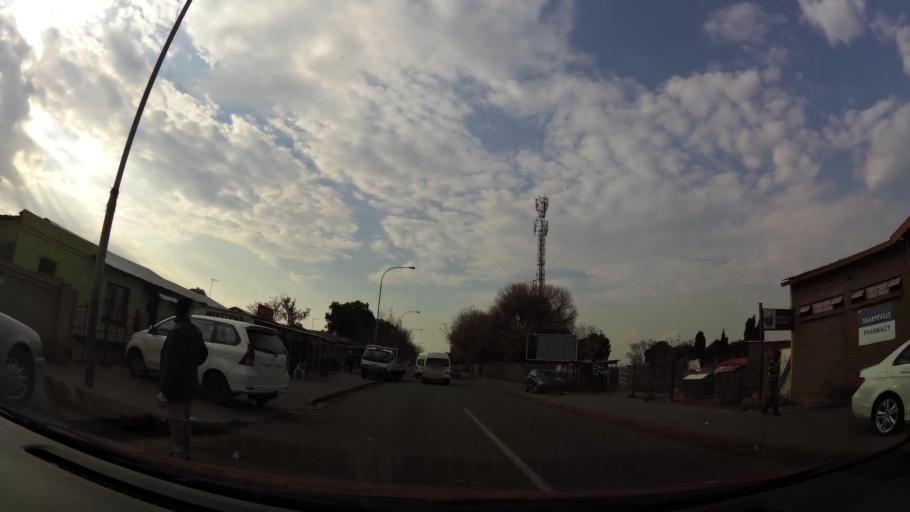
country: ZA
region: Gauteng
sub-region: Sedibeng District Municipality
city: Vanderbijlpark
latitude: -26.6935
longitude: 27.8663
